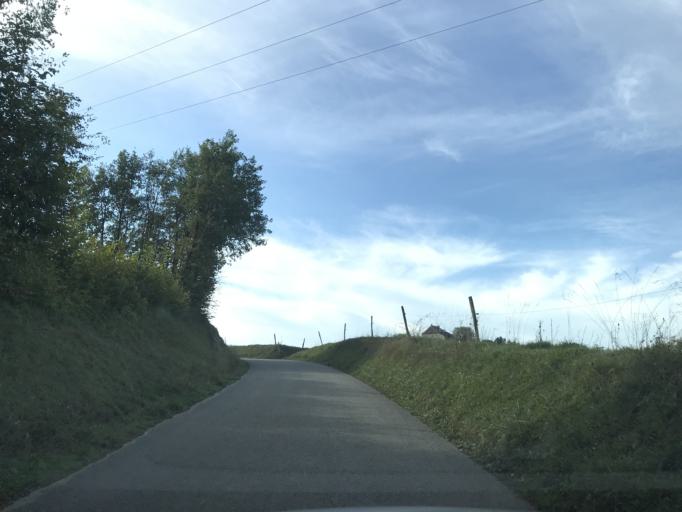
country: FR
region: Rhone-Alpes
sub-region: Departement de la Savoie
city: Yenne
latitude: 45.6880
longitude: 5.7949
